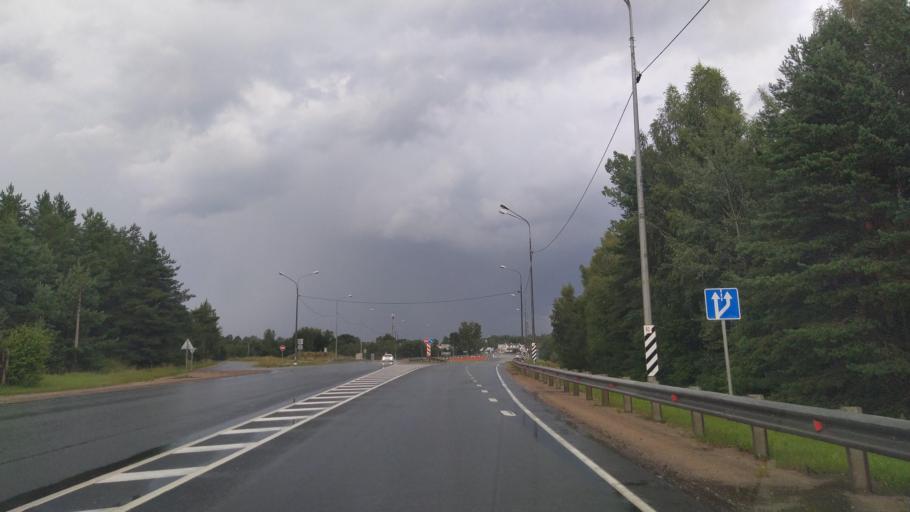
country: RU
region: Pskov
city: Pskov
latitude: 57.7399
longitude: 28.3658
